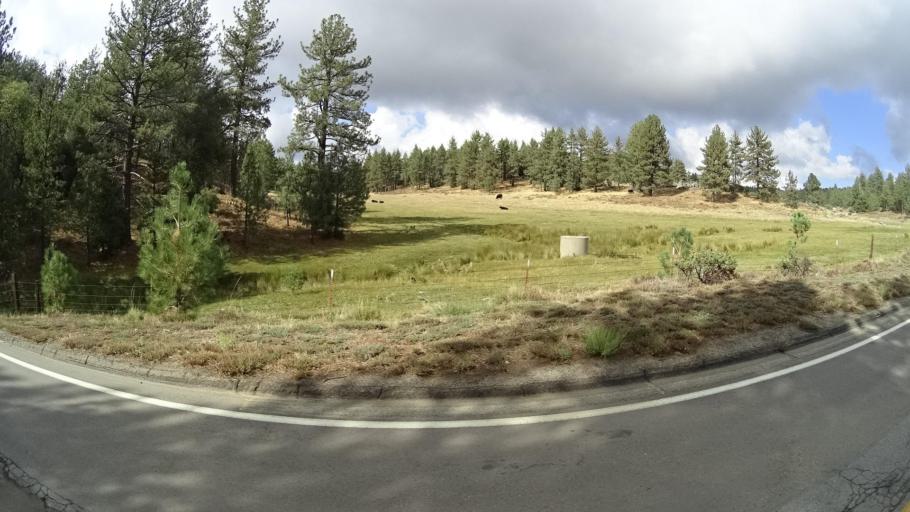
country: US
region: California
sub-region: San Diego County
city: Pine Valley
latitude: 32.8524
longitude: -116.4801
